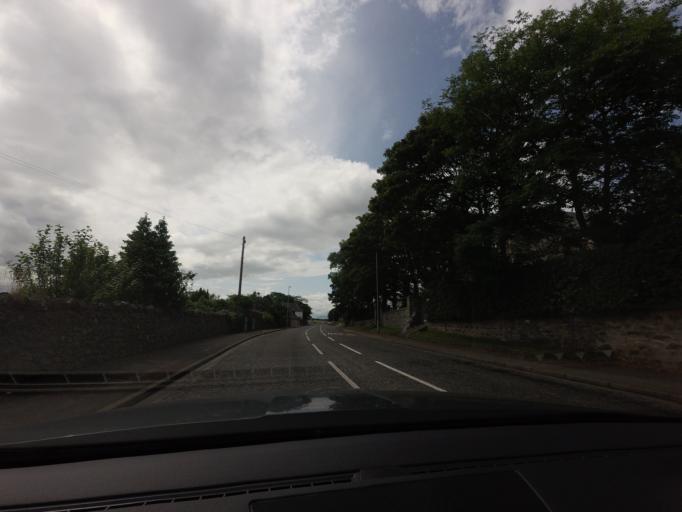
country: GB
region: Scotland
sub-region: Aberdeenshire
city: Portsoy
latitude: 57.6809
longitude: -2.6936
